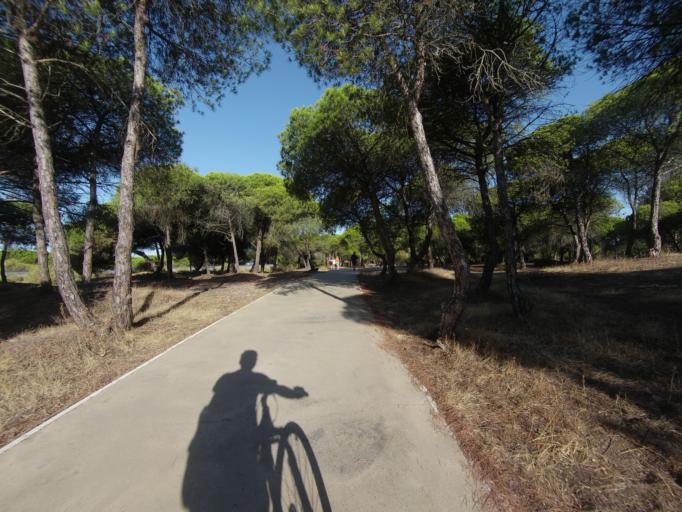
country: ES
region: Andalusia
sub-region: Provincia de Huelva
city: Aljaraque
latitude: 37.2073
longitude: -7.0331
